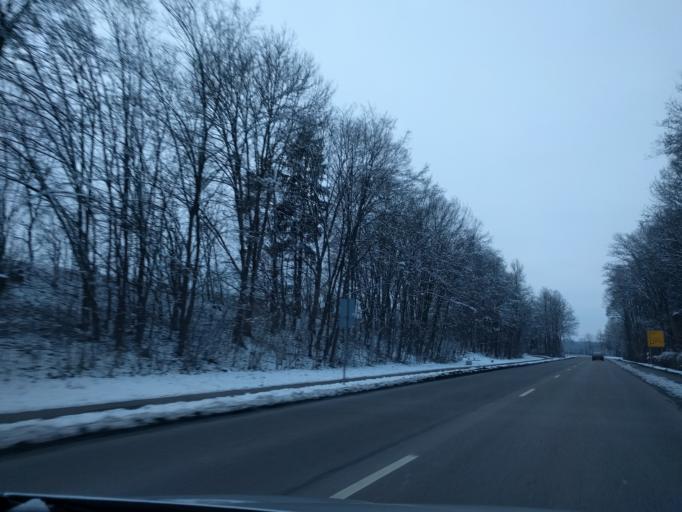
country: DE
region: Bavaria
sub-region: Swabia
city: Rain
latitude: 48.6995
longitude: 10.9059
